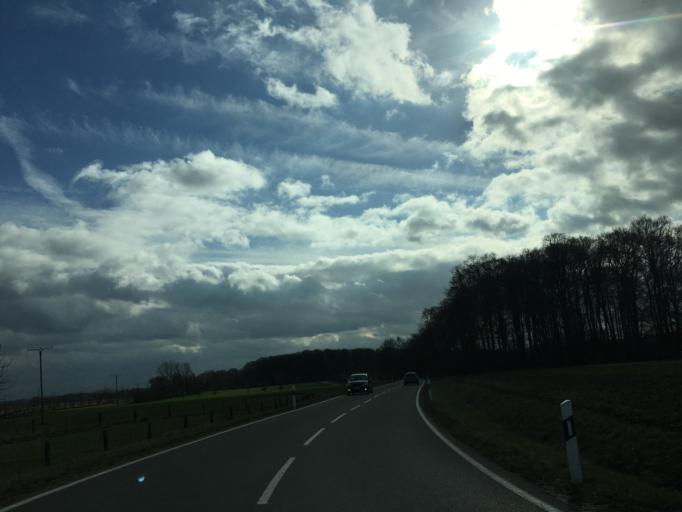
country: DE
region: North Rhine-Westphalia
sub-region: Regierungsbezirk Munster
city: Laer
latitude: 52.0280
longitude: 7.3295
